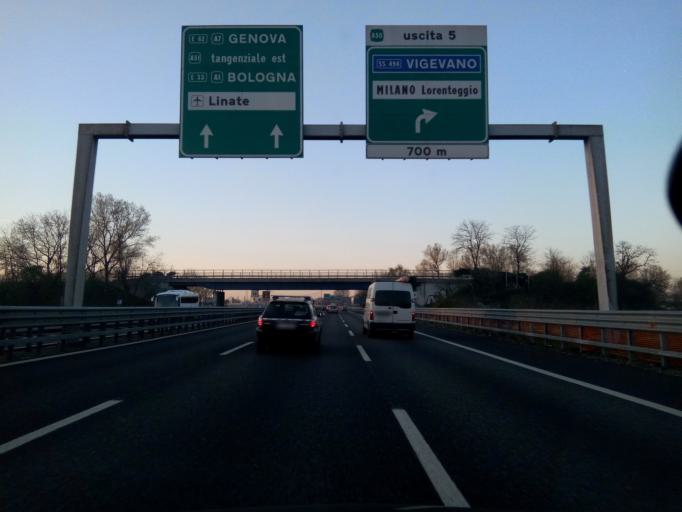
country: IT
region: Lombardy
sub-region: Citta metropolitana di Milano
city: Trezzano sul Naviglio
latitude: 45.4367
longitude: 9.0740
